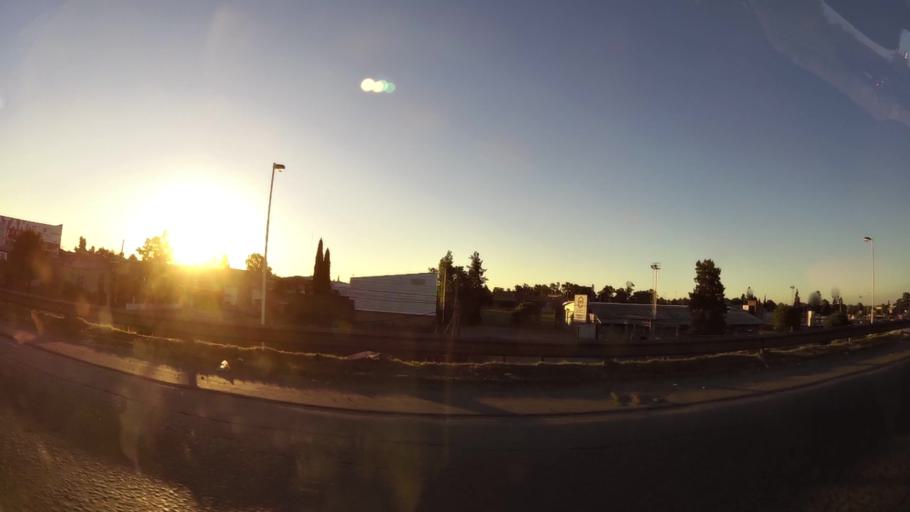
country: AR
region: Buenos Aires
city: Pontevedra
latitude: -34.7621
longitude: -58.6165
